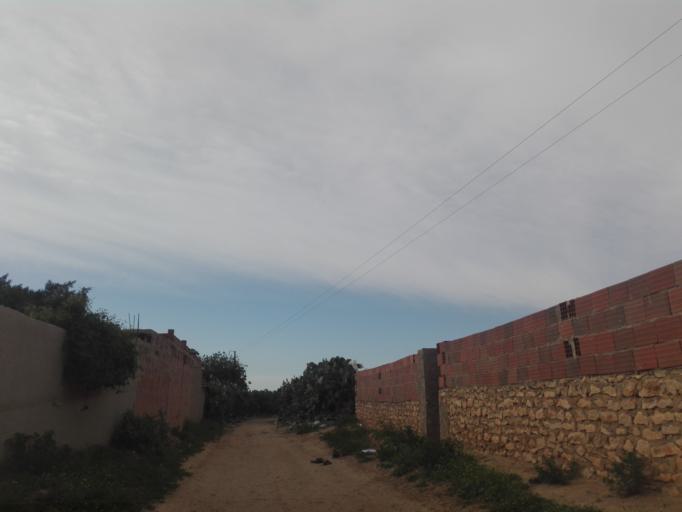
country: TN
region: Safaqis
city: Sfax
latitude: 34.7378
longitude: 10.5064
